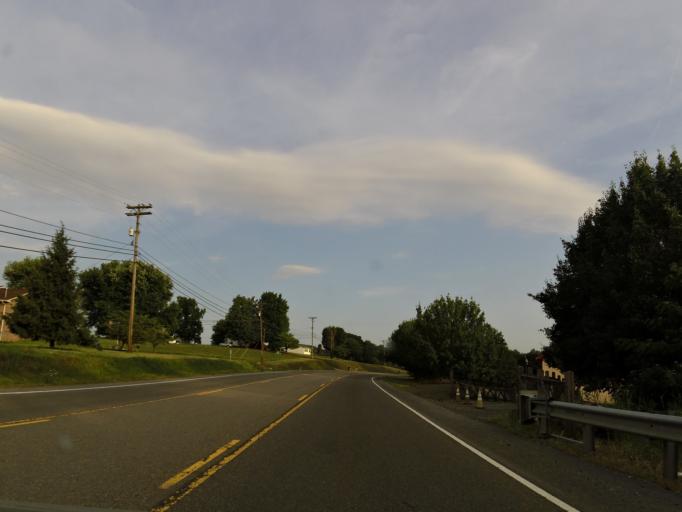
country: US
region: Tennessee
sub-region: Knox County
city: Mascot
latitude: 36.0037
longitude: -83.8226
